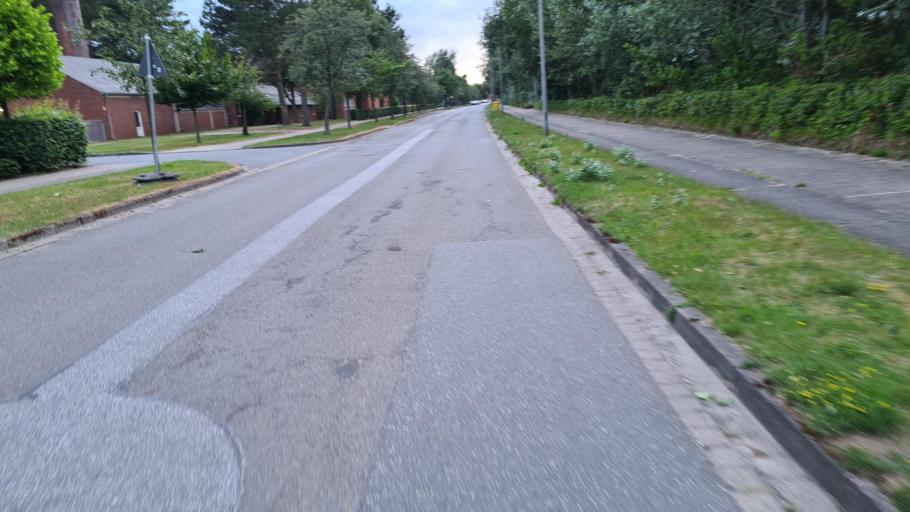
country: DE
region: Schleswig-Holstein
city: Sankt Peter-Ording
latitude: 54.2936
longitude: 8.6512
